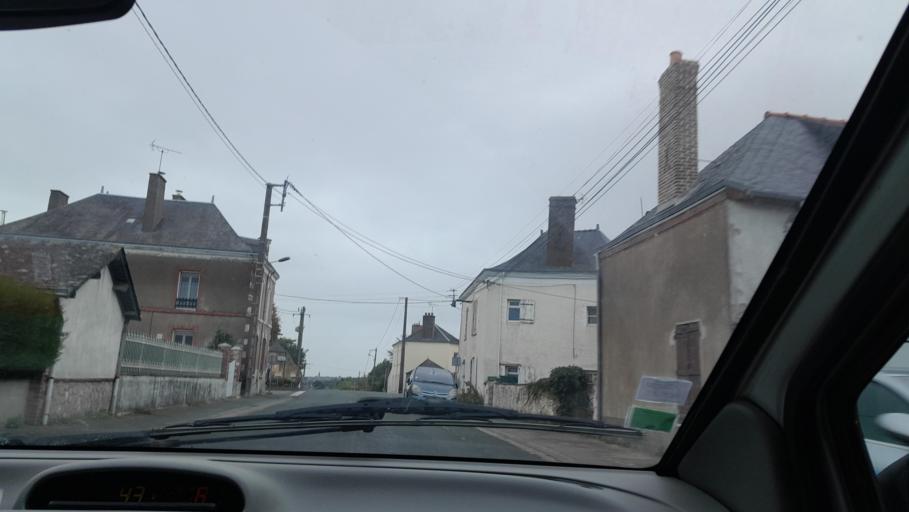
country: FR
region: Pays de la Loire
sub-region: Departement de Maine-et-Loire
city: Pouance
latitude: 47.7164
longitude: -1.1779
